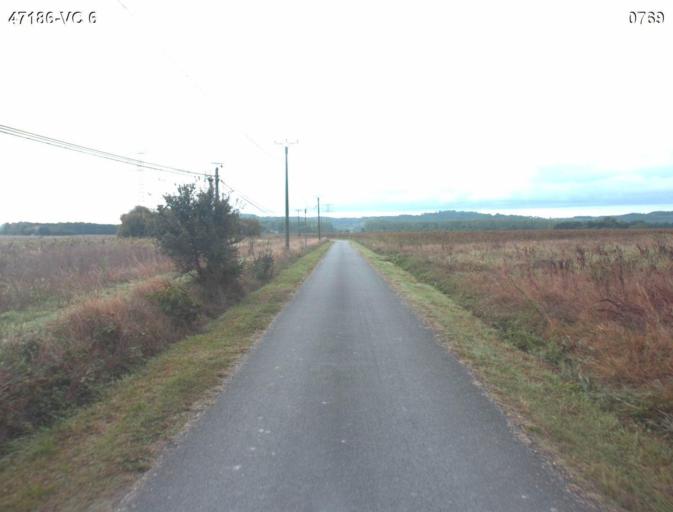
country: FR
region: Aquitaine
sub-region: Departement du Lot-et-Garonne
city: Port-Sainte-Marie
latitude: 44.2265
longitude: 0.4479
